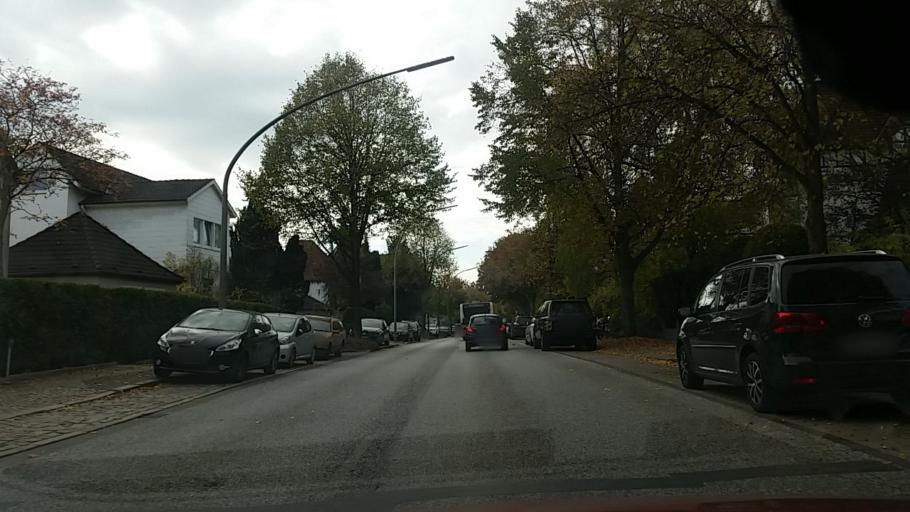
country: DE
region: Hamburg
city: Ohlsdorf
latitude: 53.6341
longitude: 10.0309
